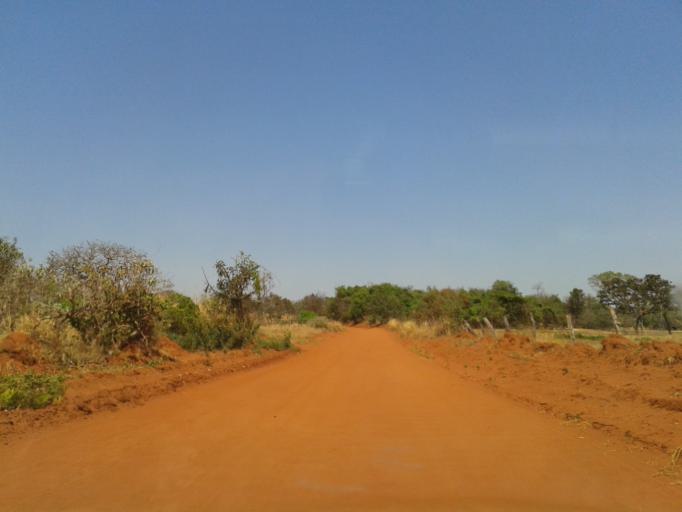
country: BR
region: Minas Gerais
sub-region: Ituiutaba
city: Ituiutaba
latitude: -19.0712
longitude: -49.3382
